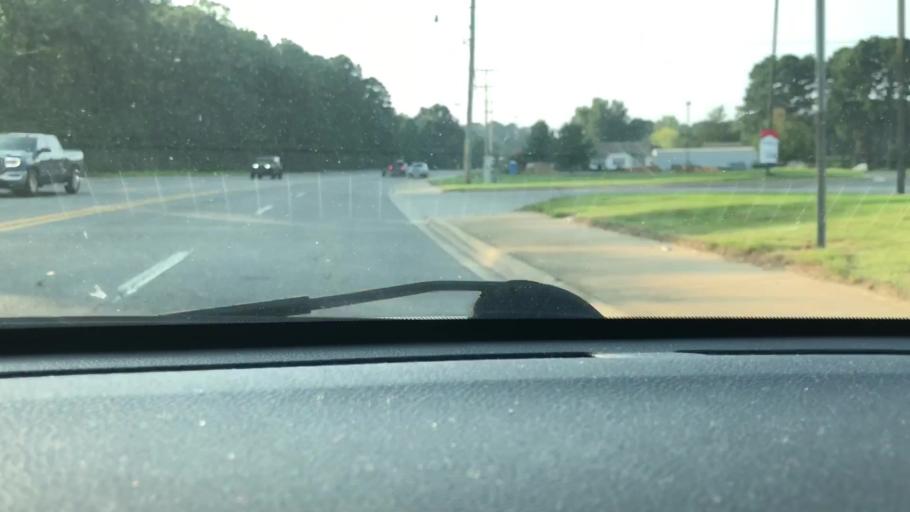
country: US
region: Arkansas
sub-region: Saline County
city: Bryant
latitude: 34.6094
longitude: -92.4931
